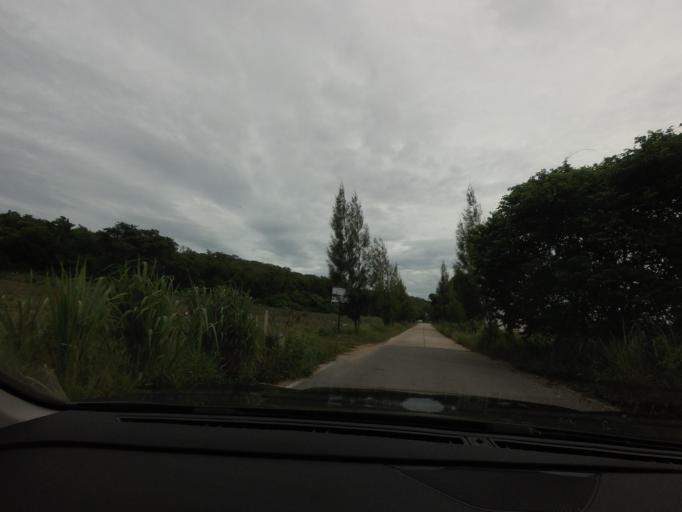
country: TH
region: Prachuap Khiri Khan
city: Hua Hin
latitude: 12.4875
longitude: 99.9424
